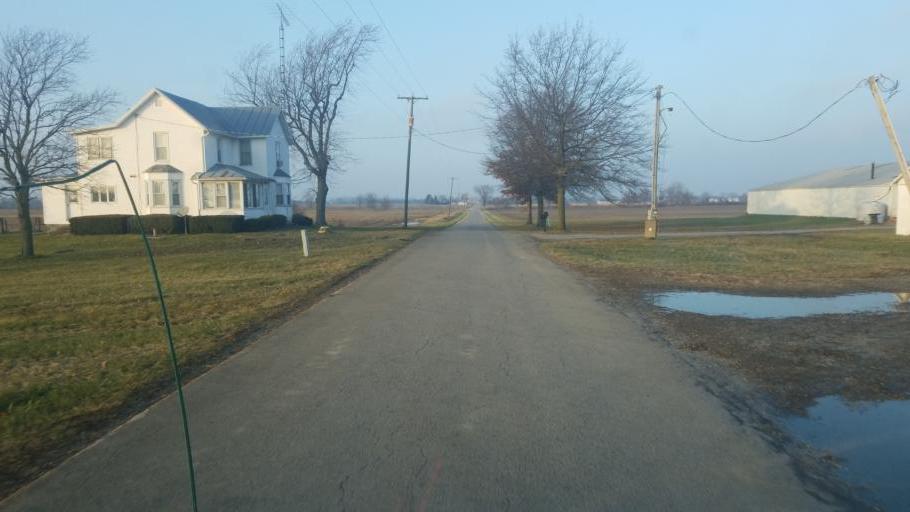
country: US
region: Ohio
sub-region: Wyandot County
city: Carey
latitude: 40.9373
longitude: -83.4290
